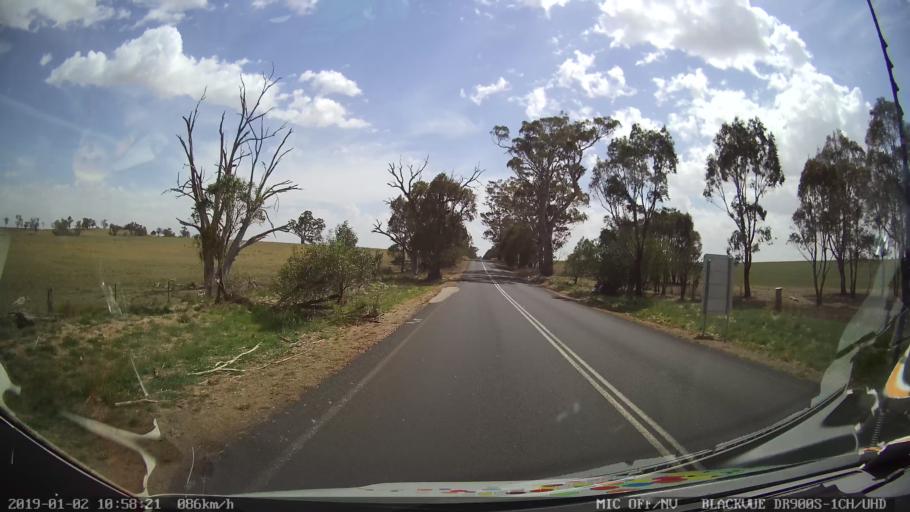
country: AU
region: New South Wales
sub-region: Cootamundra
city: Cootamundra
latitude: -34.6255
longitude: 148.2904
